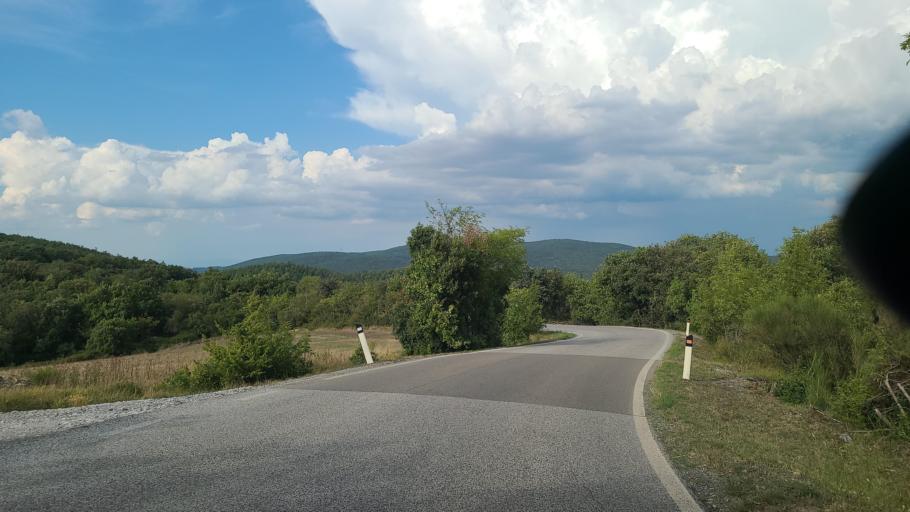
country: IT
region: Tuscany
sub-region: Provincia di Siena
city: San Gimignano
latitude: 43.4219
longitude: 10.9758
